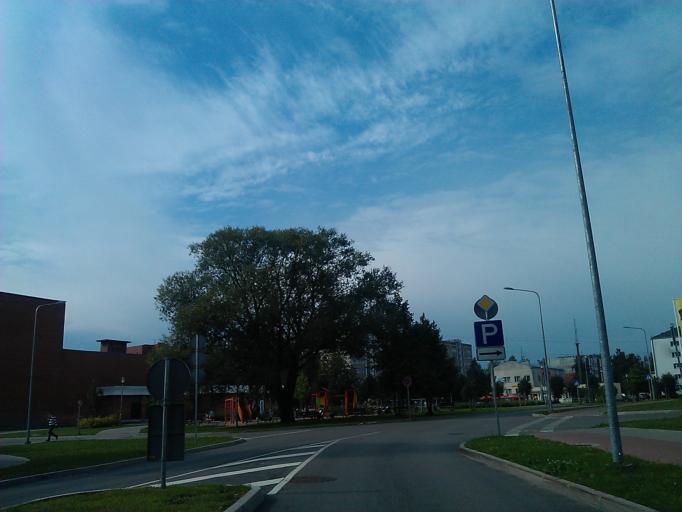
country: LV
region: Salaspils
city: Salaspils
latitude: 56.8545
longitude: 24.3377
